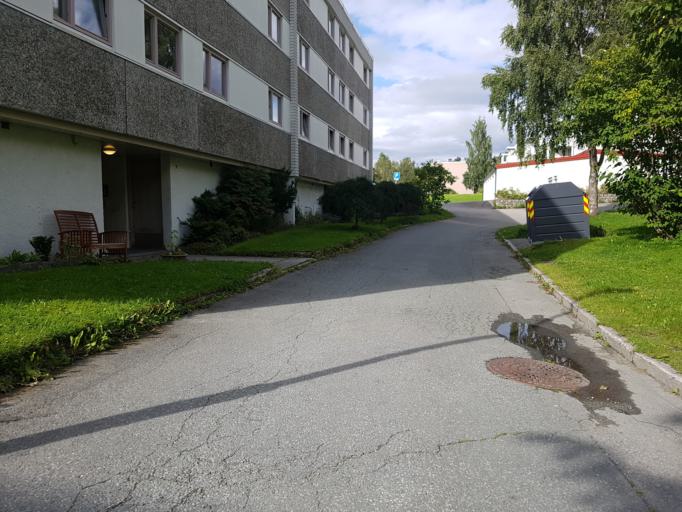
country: NO
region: Sor-Trondelag
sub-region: Trondheim
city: Trondheim
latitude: 63.4047
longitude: 10.4430
